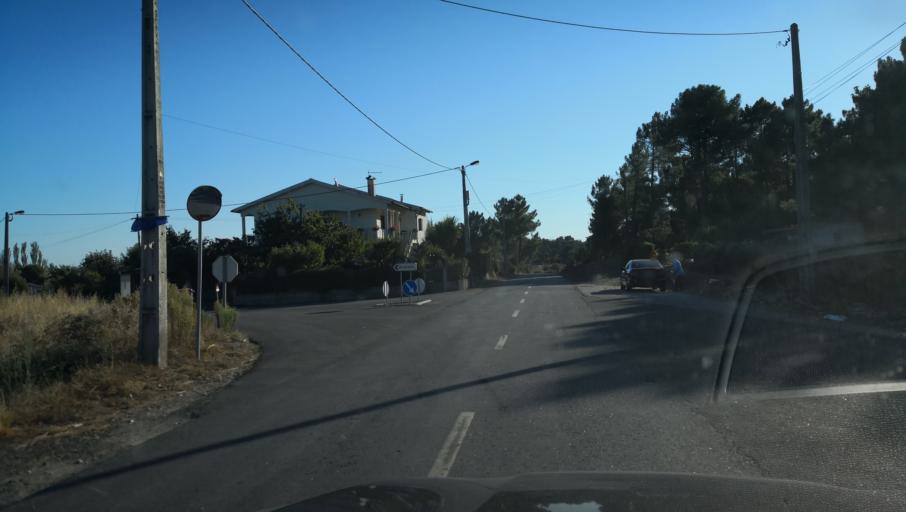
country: PT
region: Vila Real
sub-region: Vila Real
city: Vila Real
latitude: 41.2735
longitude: -7.7266
